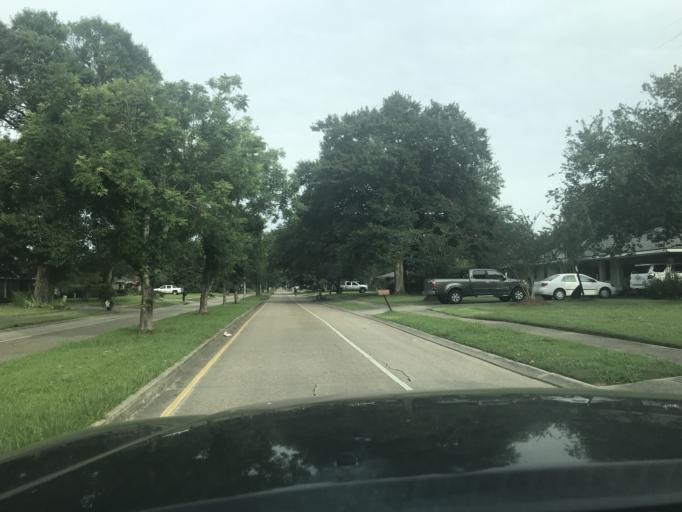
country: US
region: Louisiana
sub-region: Lafayette Parish
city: Lafayette
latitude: 30.1982
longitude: -92.0496
